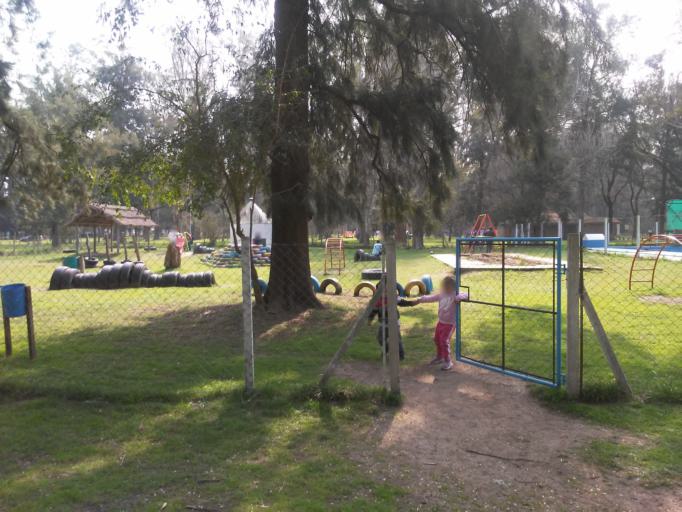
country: AR
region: Buenos Aires
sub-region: Partido de General Rodriguez
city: General Rodriguez
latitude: -34.6657
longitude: -58.8574
